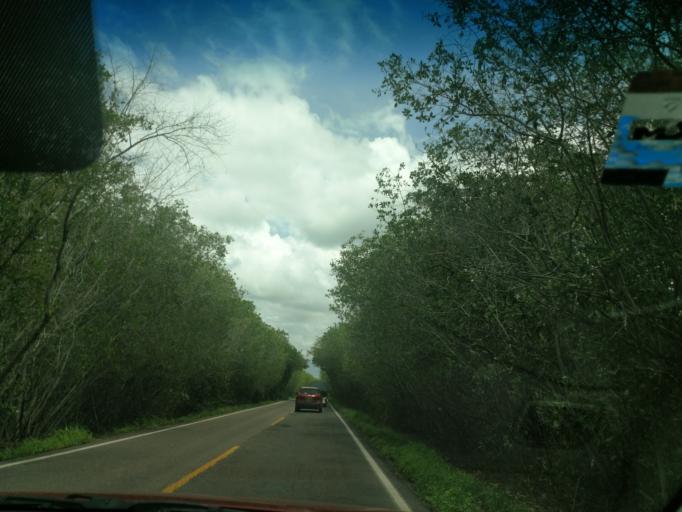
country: MX
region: Nayarit
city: San Blas
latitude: 21.5467
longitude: -105.2529
